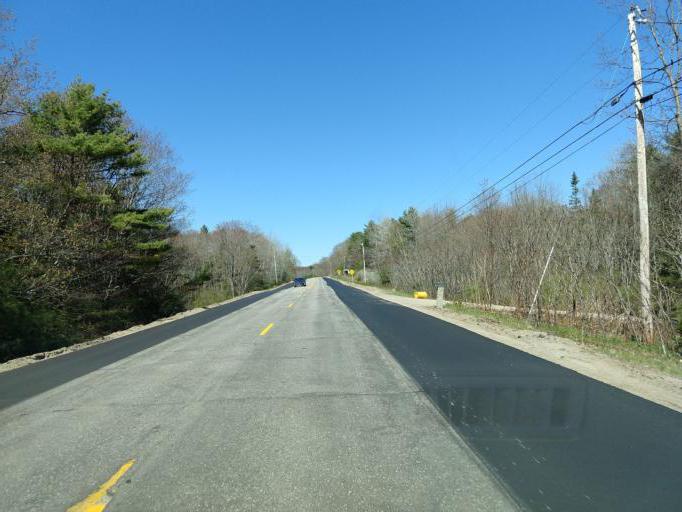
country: US
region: Maine
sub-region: York County
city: Arundel
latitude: 43.4166
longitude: -70.4110
